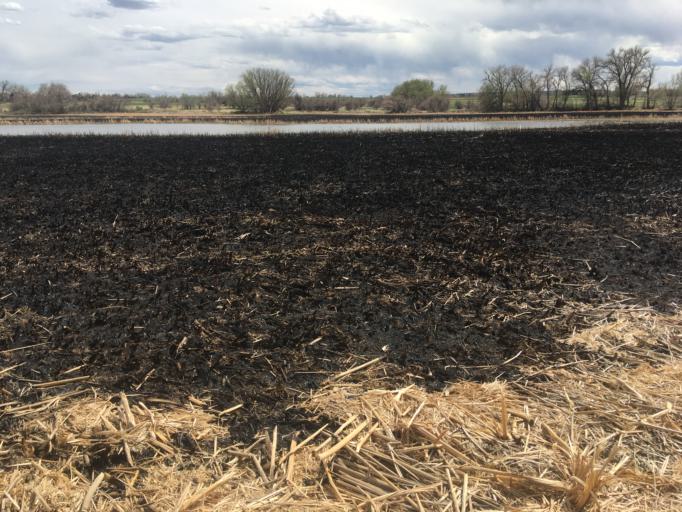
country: US
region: Colorado
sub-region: Boulder County
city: Gunbarrel
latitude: 40.0391
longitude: -105.1401
